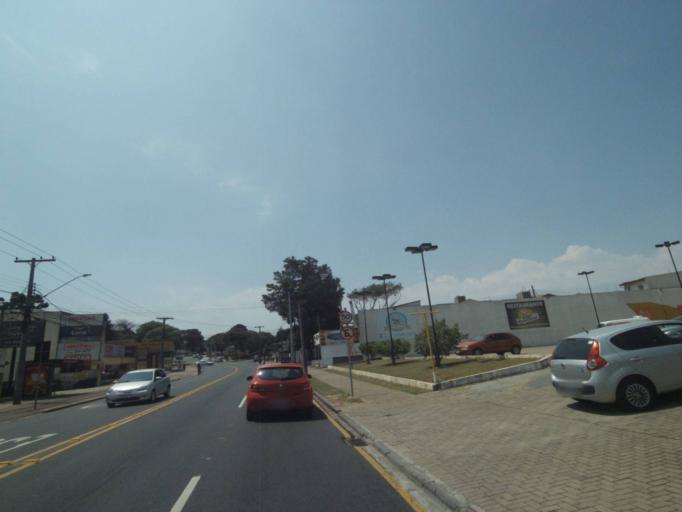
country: BR
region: Parana
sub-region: Curitiba
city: Curitiba
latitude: -25.4773
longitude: -49.3091
